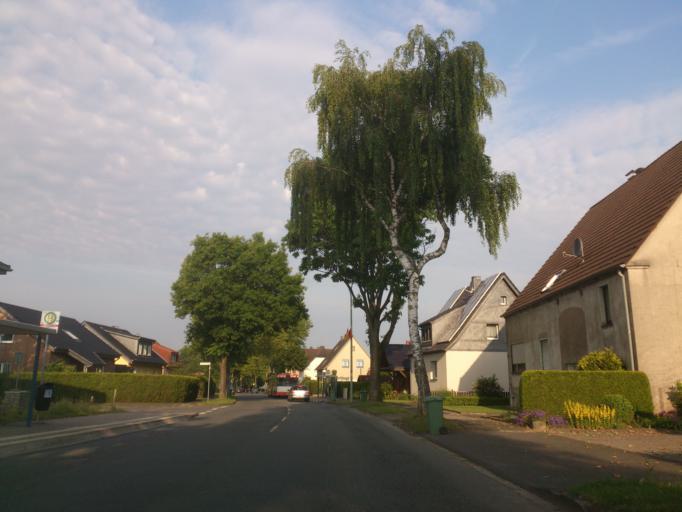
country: DE
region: North Rhine-Westphalia
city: Bad Lippspringe
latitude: 51.7418
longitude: 8.8328
